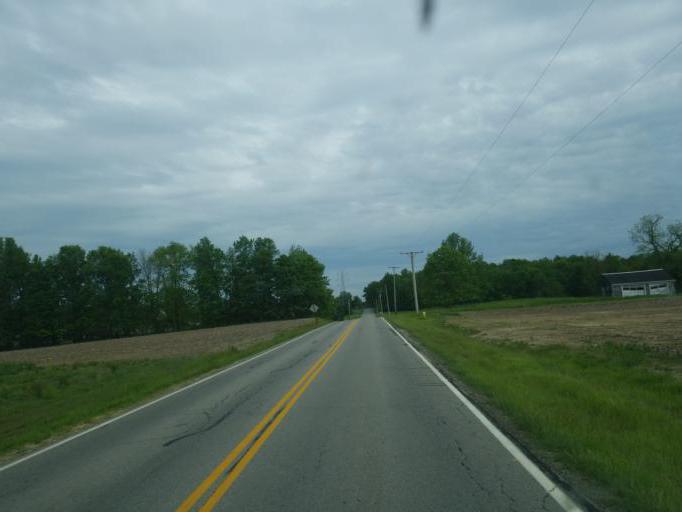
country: US
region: Ohio
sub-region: Richland County
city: Ontario
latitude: 40.7769
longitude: -82.6291
